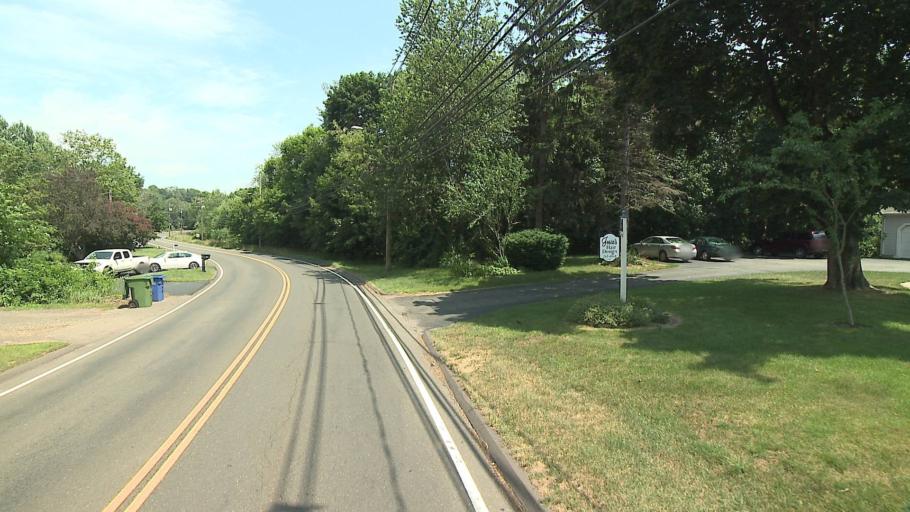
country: US
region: Connecticut
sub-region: New Haven County
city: Wallingford Center
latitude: 41.4469
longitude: -72.8001
